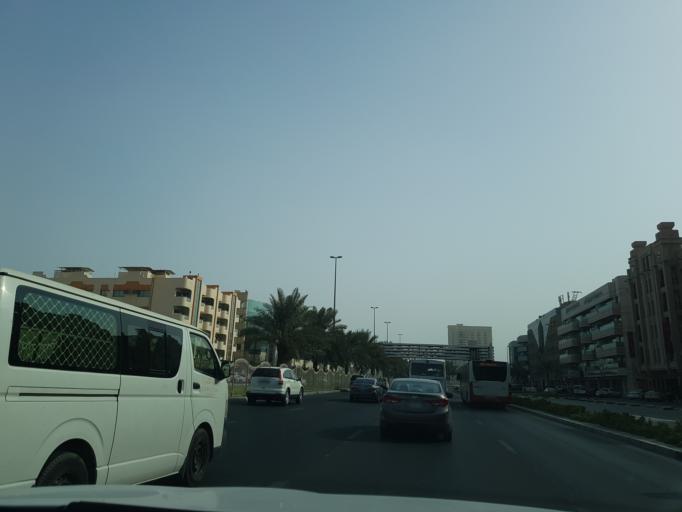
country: AE
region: Ash Shariqah
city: Sharjah
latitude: 25.2434
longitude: 55.2763
